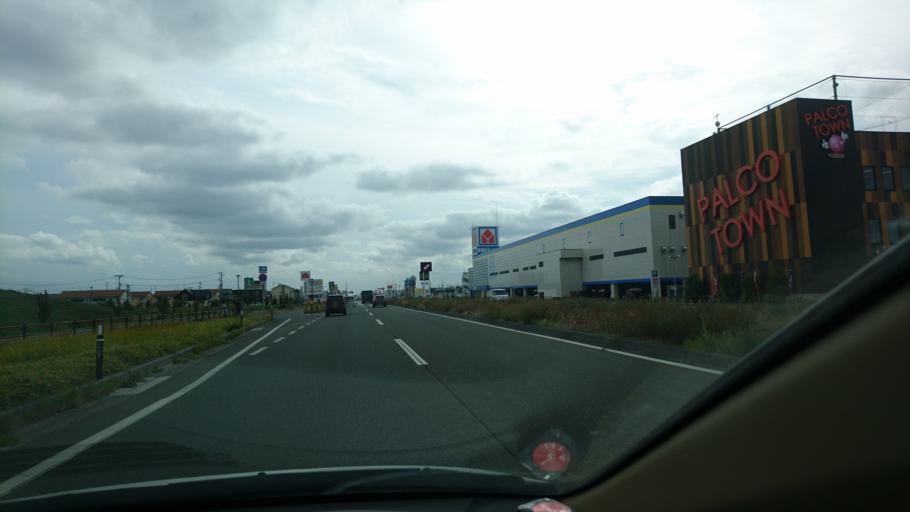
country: JP
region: Iwate
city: Morioka-shi
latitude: 39.6802
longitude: 141.1355
